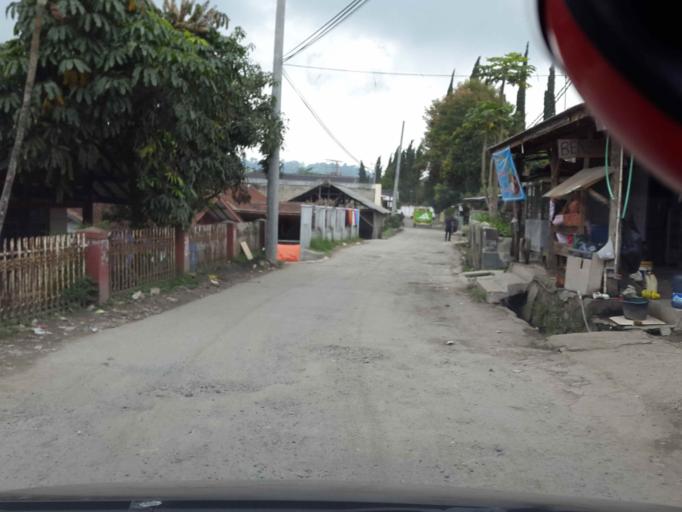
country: ID
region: West Java
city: Lembang
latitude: -6.8098
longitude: 107.6456
